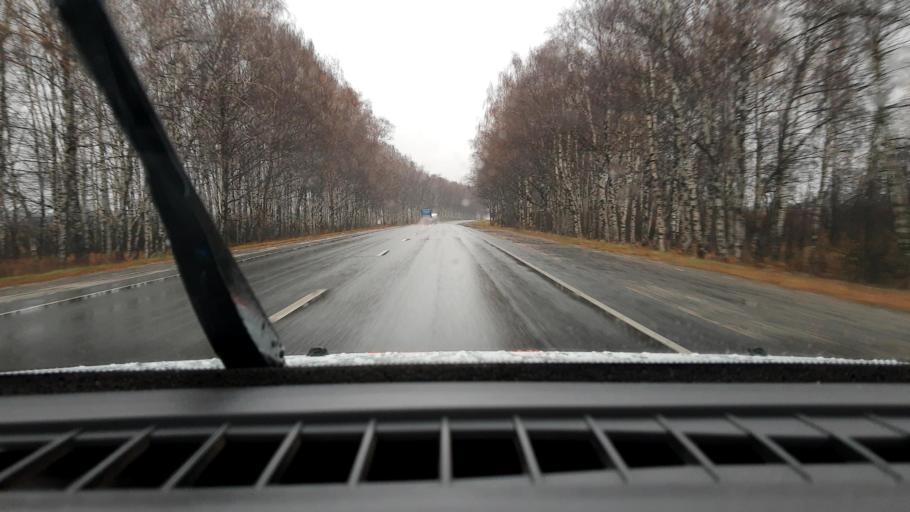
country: RU
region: Nizjnij Novgorod
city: Sitniki
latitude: 56.5351
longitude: 44.0220
